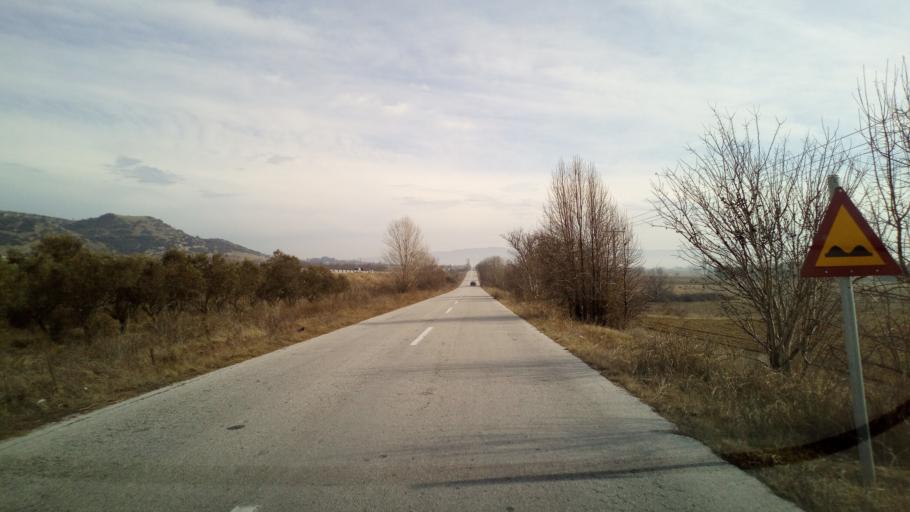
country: GR
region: Central Macedonia
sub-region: Nomos Thessalonikis
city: Gerakarou
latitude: 40.7019
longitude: 23.2000
